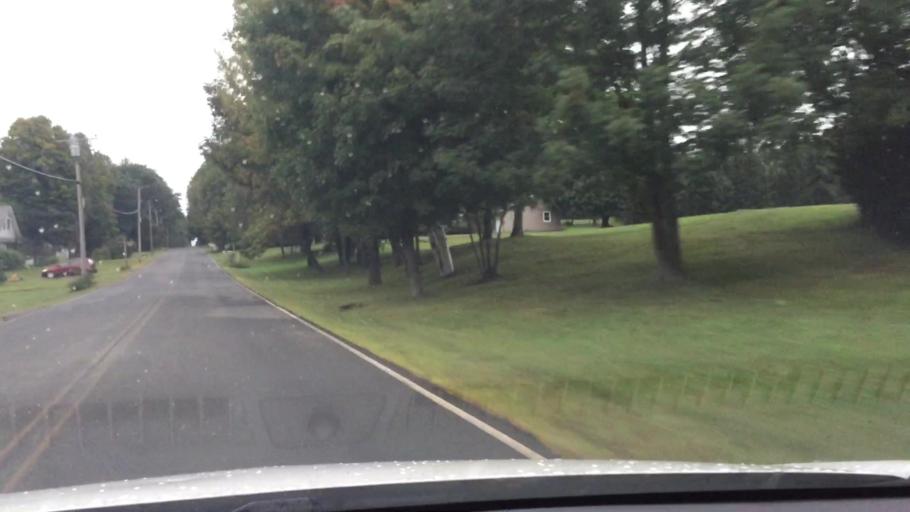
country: US
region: Massachusetts
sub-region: Berkshire County
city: Otis
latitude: 42.2035
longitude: -72.9394
